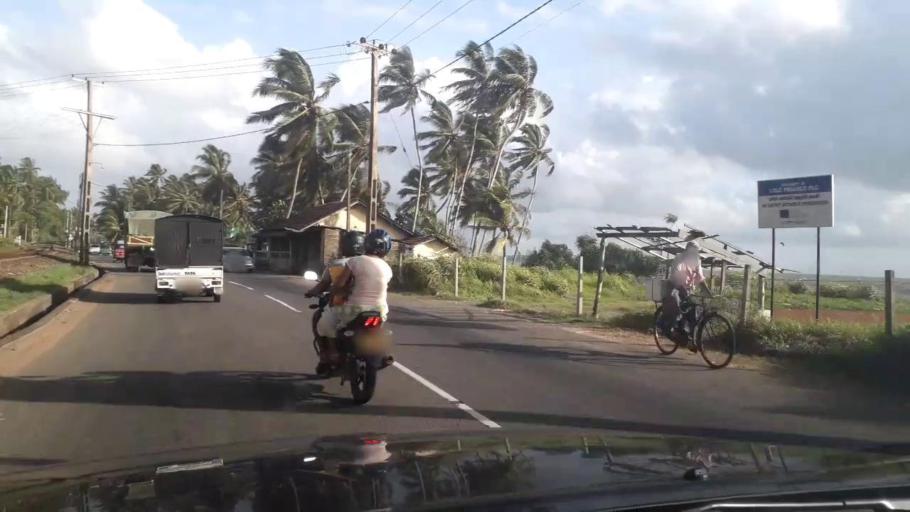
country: LK
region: Western
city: Beruwala
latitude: 6.4972
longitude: 79.9810
